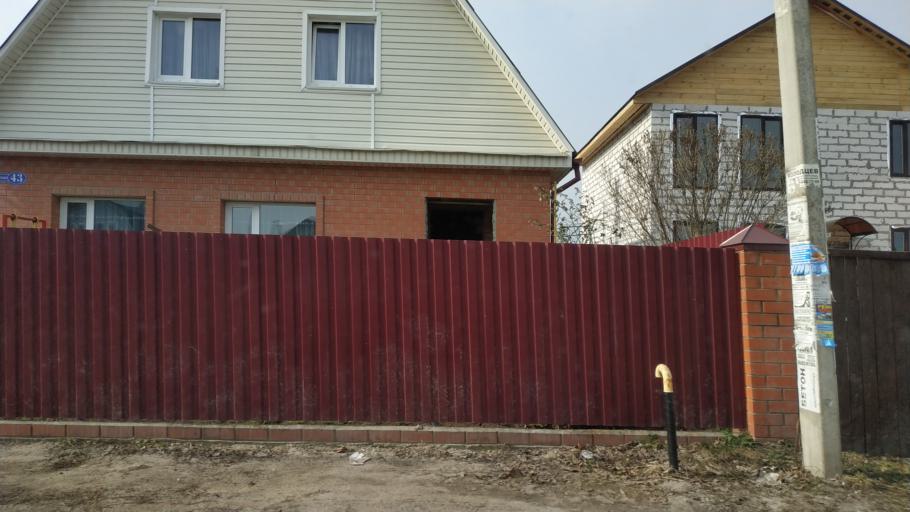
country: RU
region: Moskovskaya
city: Beloozerskiy
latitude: 55.4357
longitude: 38.4866
